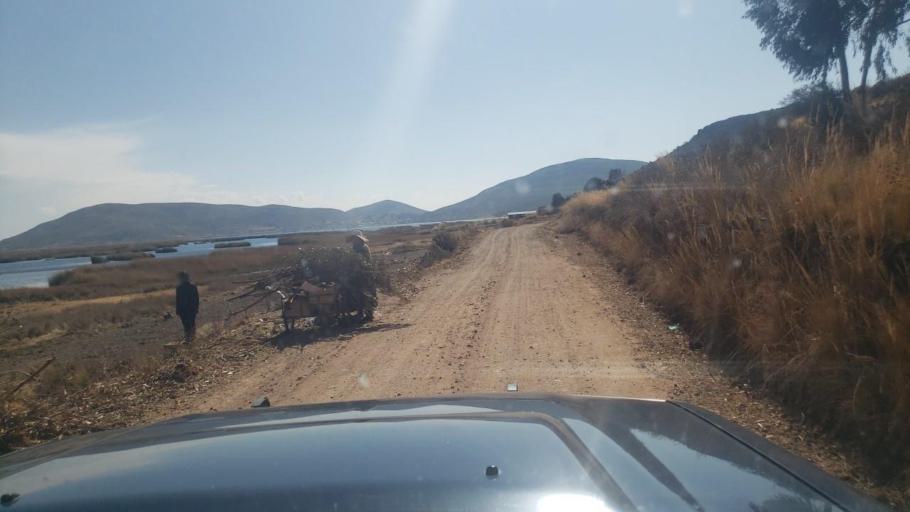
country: BO
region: La Paz
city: Huatajata
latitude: -16.3394
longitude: -68.6836
